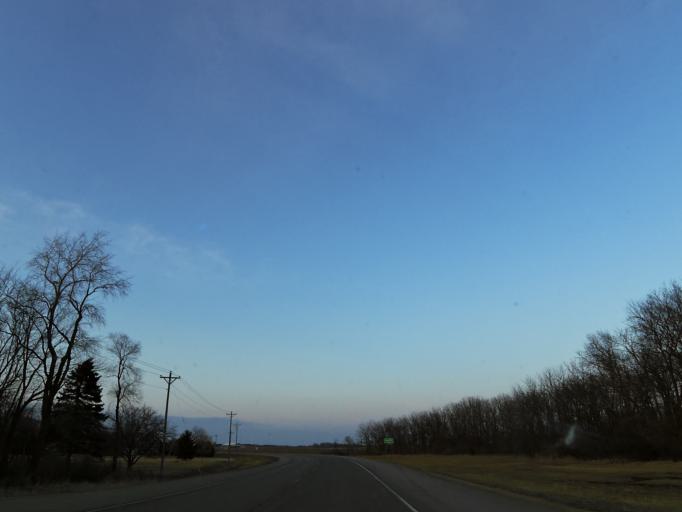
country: US
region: Minnesota
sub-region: Mower County
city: Austin
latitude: 43.6594
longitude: -92.9415
